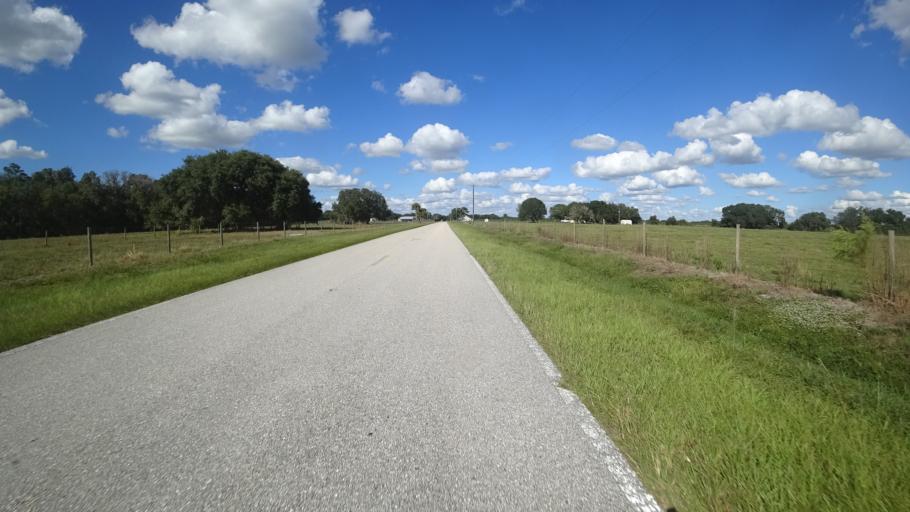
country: US
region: Florida
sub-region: Sarasota County
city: North Port
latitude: 27.2019
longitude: -82.1222
